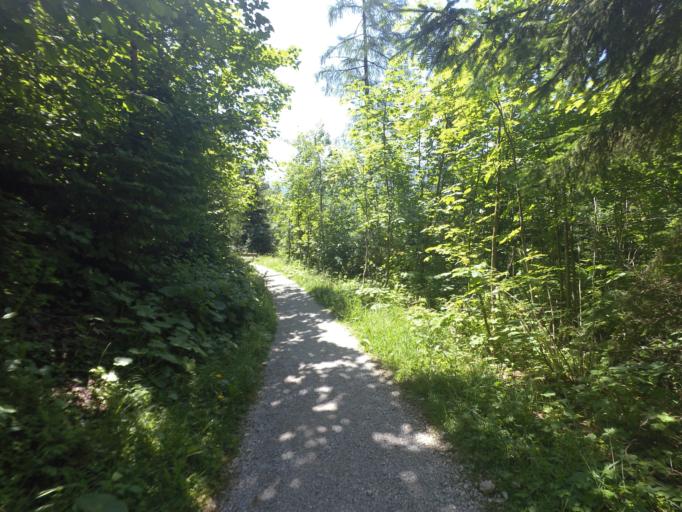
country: AT
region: Salzburg
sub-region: Politischer Bezirk Zell am See
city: Leogang
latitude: 47.4601
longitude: 12.7492
